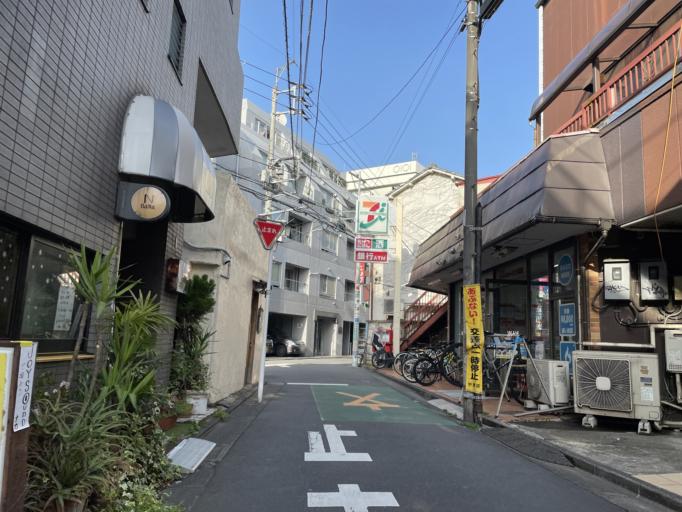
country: JP
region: Tokyo
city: Tokyo
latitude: 35.7039
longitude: 139.6633
